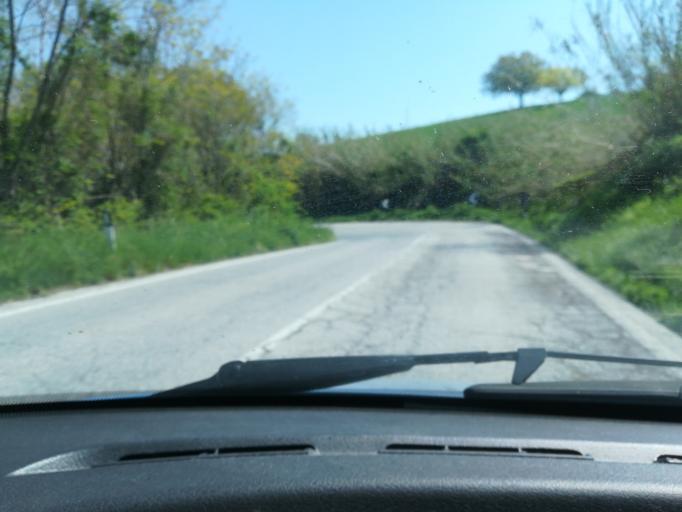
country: IT
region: The Marches
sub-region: Provincia di Macerata
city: Cingoli
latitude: 43.3894
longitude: 13.2055
